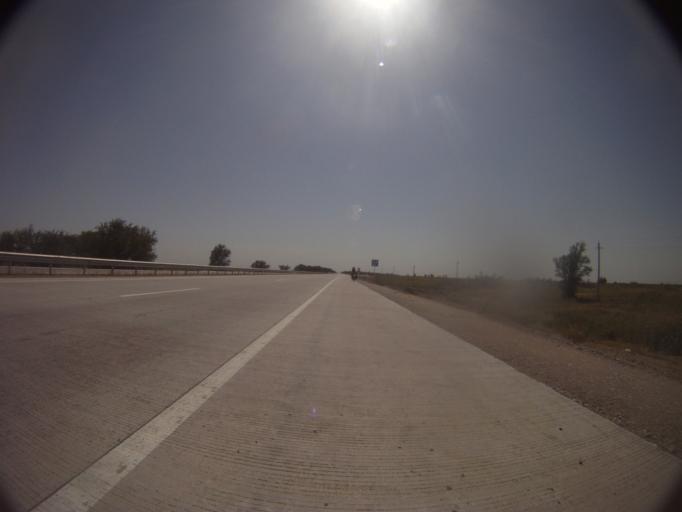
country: KZ
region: Ongtustik Qazaqstan
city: Bayaldyr
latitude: 43.0916
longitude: 68.6388
